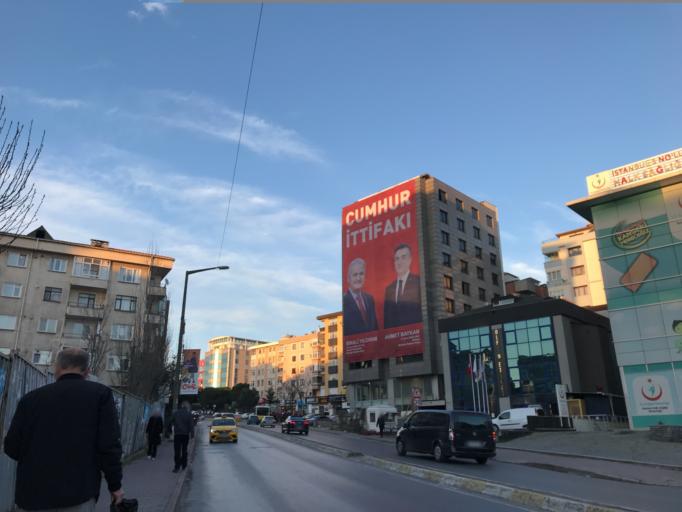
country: TR
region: Istanbul
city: Maltepe
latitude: 40.9330
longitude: 29.1370
